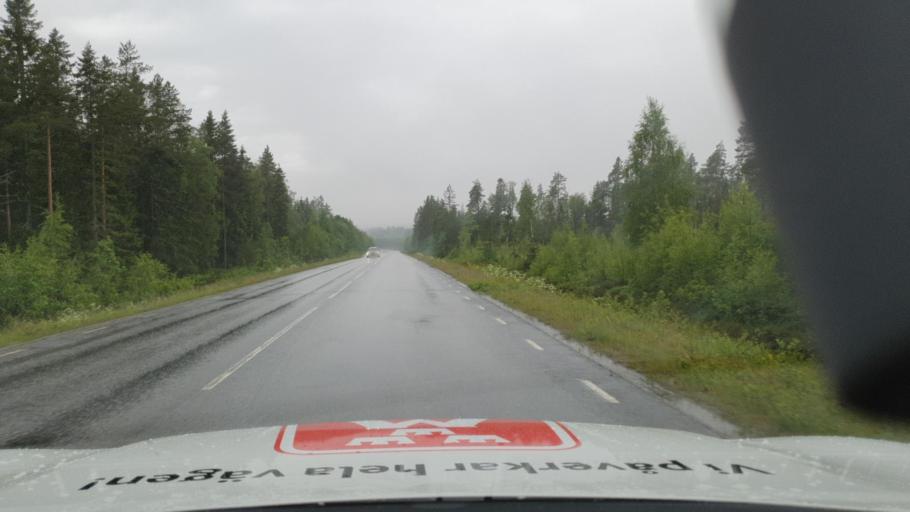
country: SE
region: Vaesterbotten
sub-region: Umea Kommun
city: Roback
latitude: 63.7859
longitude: 20.1098
